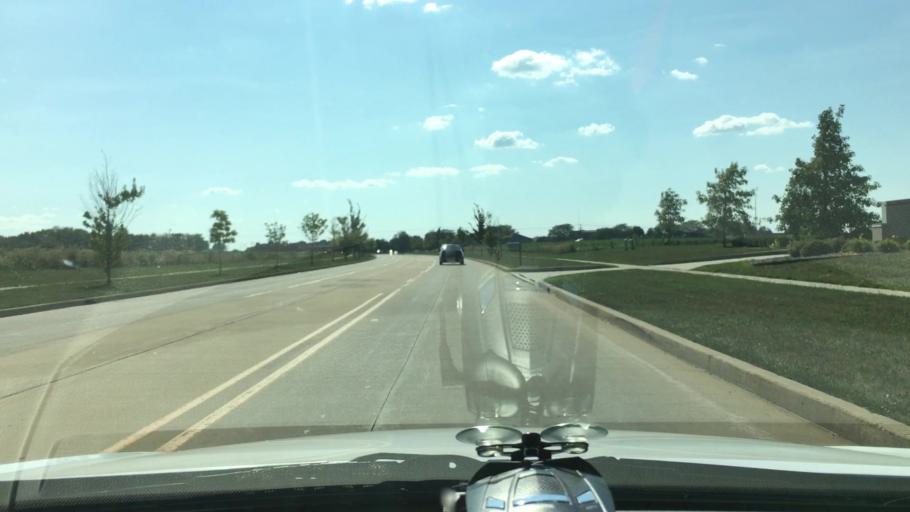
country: US
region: Illinois
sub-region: Champaign County
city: Champaign
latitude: 40.1491
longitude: -88.2629
